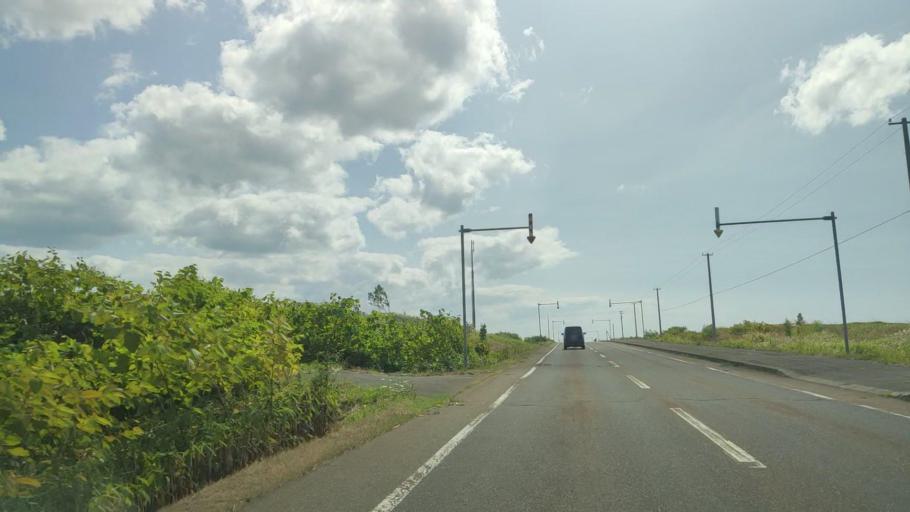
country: JP
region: Hokkaido
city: Makubetsu
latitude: 44.7895
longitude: 141.7903
